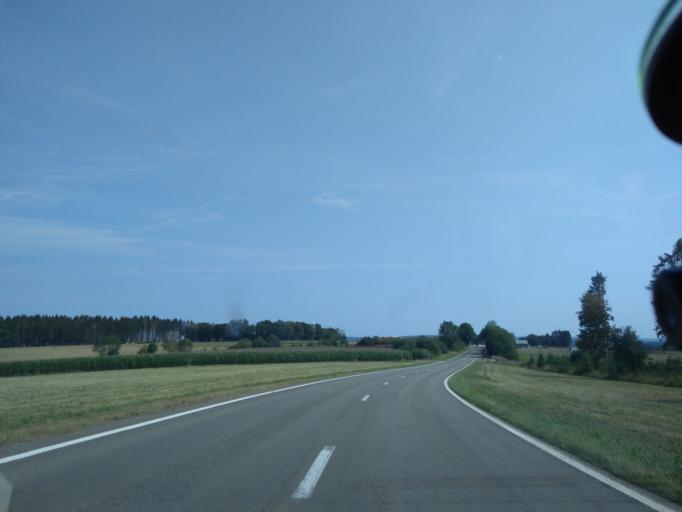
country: BE
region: Wallonia
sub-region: Province du Luxembourg
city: Tenneville
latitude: 50.1438
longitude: 5.5031
